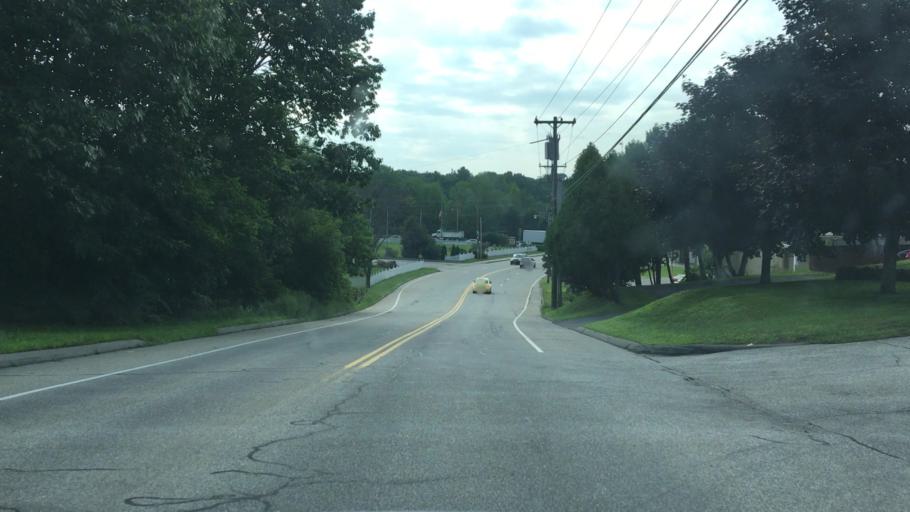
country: US
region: Maine
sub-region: Androscoggin County
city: Lewiston
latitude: 44.0786
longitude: -70.1820
